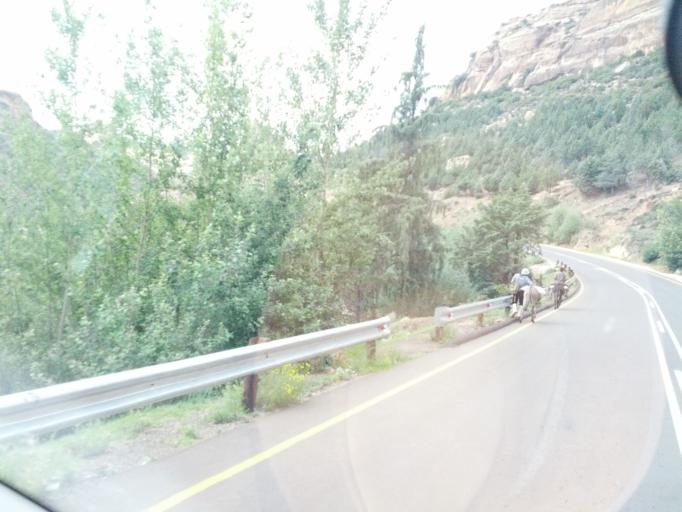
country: LS
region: Maseru
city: Nako
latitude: -29.4758
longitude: 27.7386
